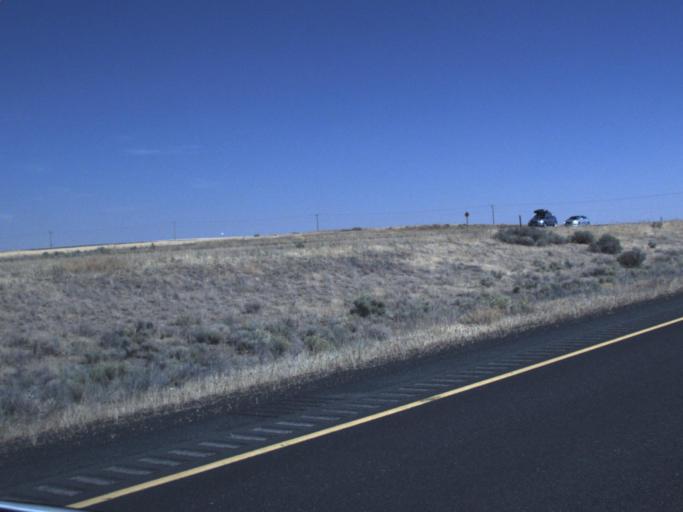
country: US
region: Washington
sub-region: Grant County
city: Warden
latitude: 47.0859
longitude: -118.8161
